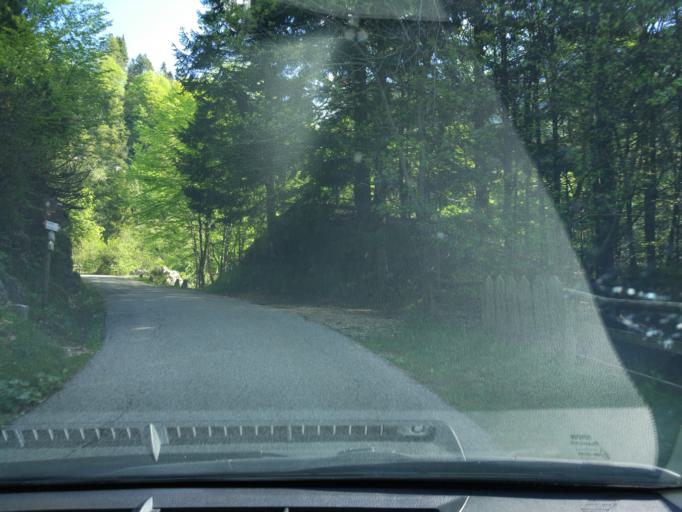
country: IT
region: Veneto
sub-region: Provincia di Verona
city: Selva di Progno
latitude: 45.6892
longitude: 11.1200
